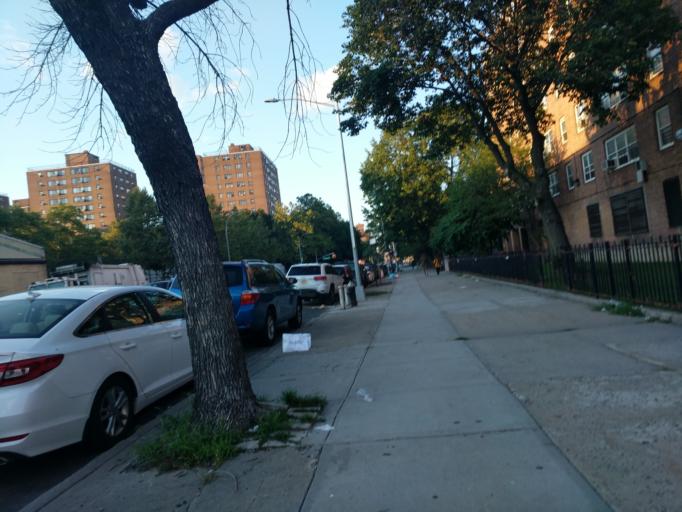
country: US
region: New York
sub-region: Queens County
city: Long Island City
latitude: 40.7619
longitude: -73.9347
